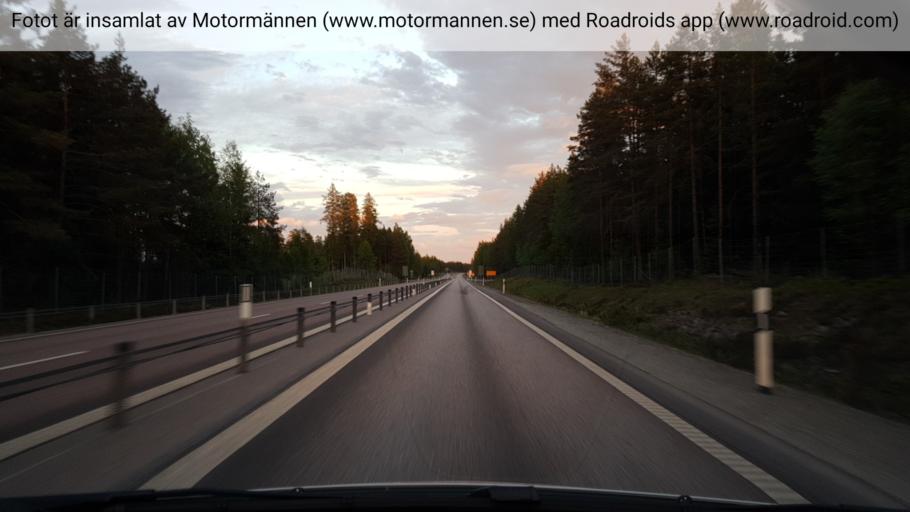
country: SE
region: Vaestmanland
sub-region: Surahammars Kommun
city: Ramnas
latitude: 59.8219
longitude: 16.1075
